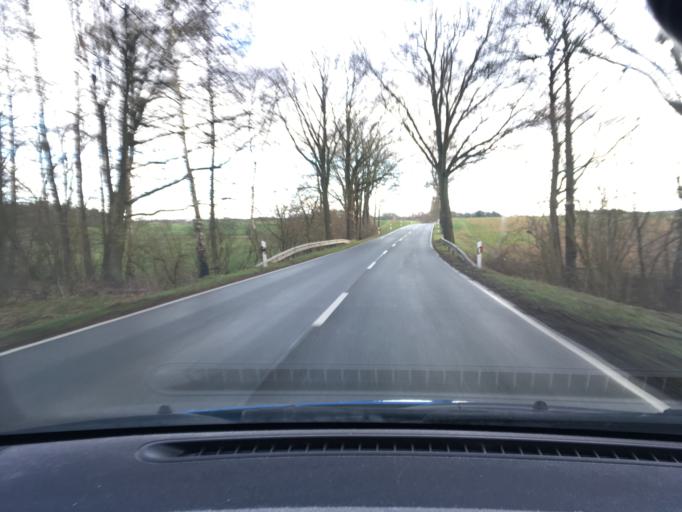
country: DE
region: Lower Saxony
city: Egestorf
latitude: 53.2209
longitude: 10.0264
